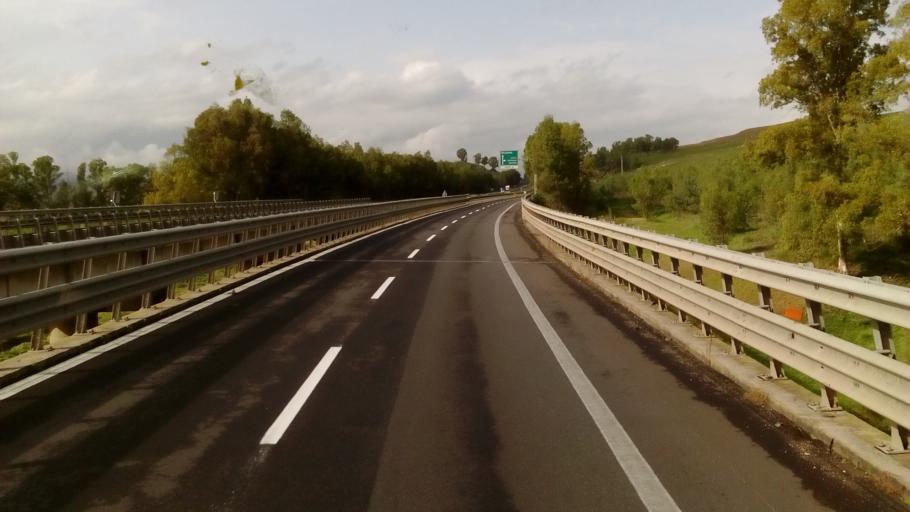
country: IT
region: Sicily
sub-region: Catania
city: Raddusa
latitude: 37.5423
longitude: 14.5497
